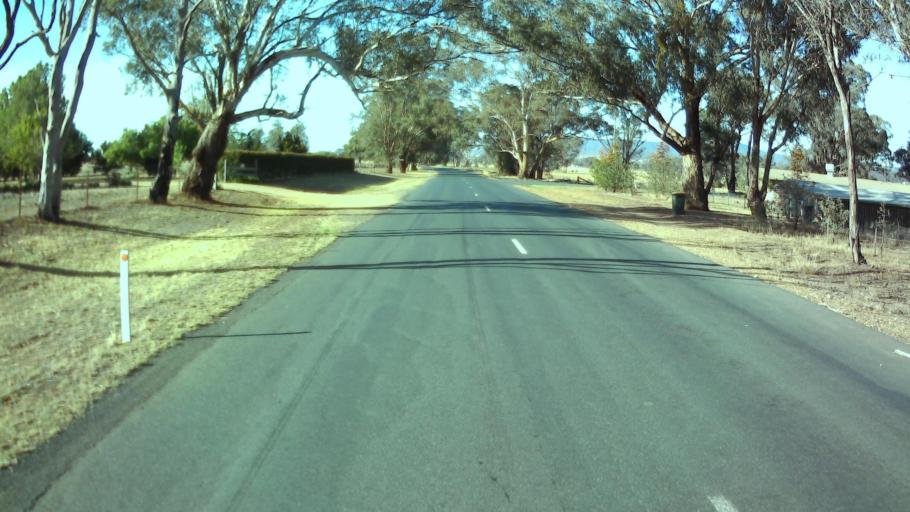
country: AU
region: New South Wales
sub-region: Weddin
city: Grenfell
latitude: -33.9138
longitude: 148.1433
